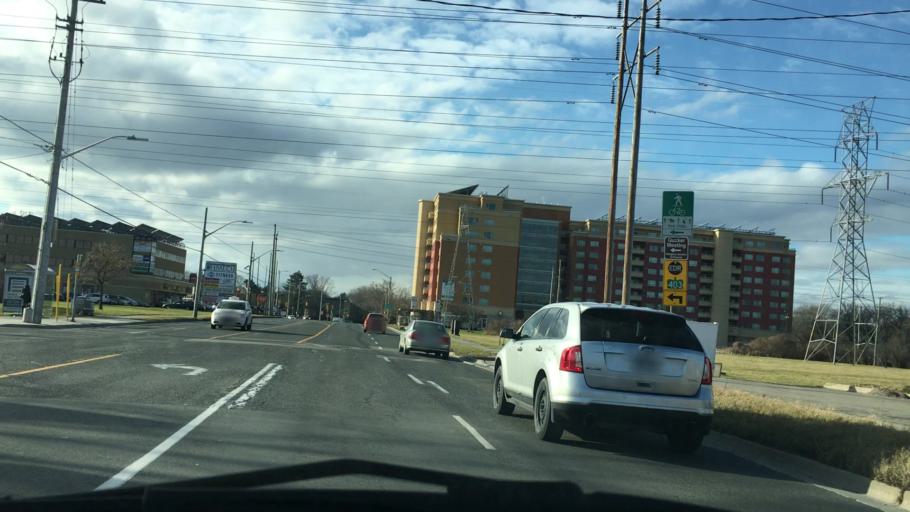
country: CA
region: Ontario
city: Ancaster
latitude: 43.2574
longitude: -79.9319
